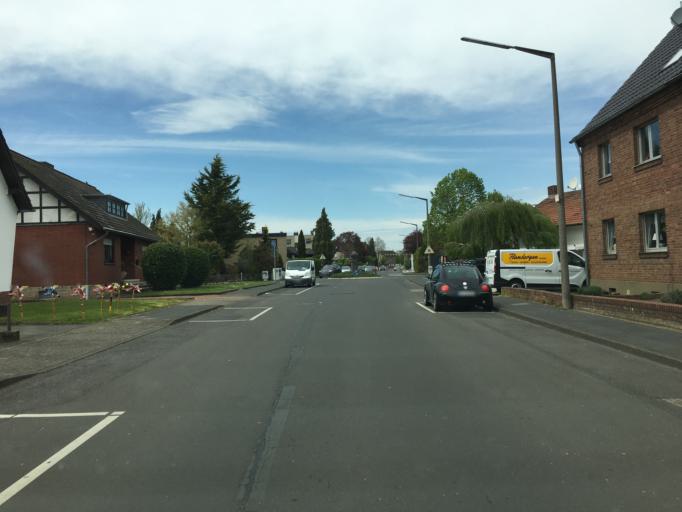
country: DE
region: North Rhine-Westphalia
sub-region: Regierungsbezirk Koln
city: Erftstadt
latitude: 50.8093
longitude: 6.8030
